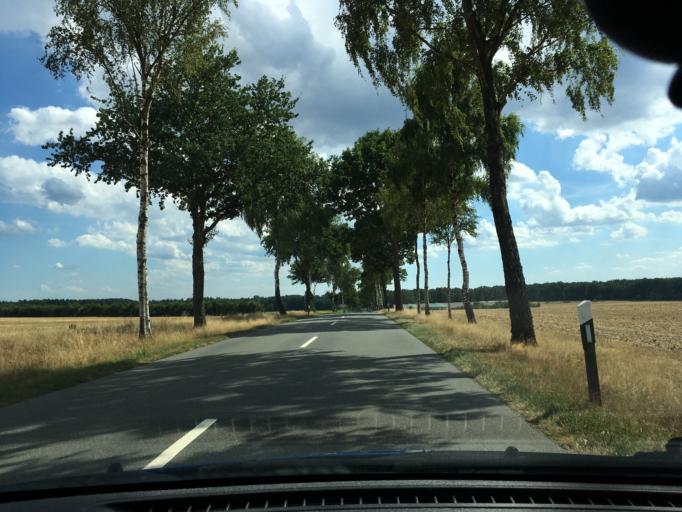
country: DE
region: Lower Saxony
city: Rehlingen
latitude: 53.0724
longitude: 10.2322
